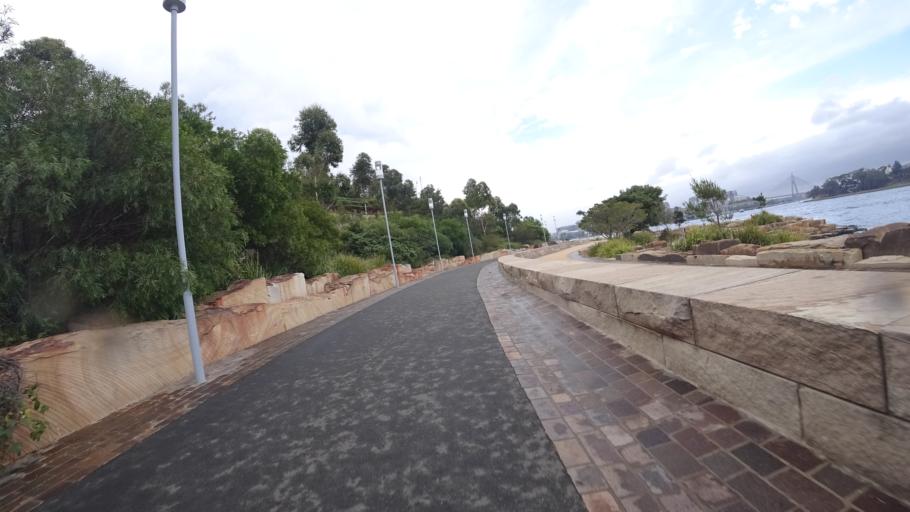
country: AU
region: New South Wales
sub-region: Leichhardt
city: Balmain East
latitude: -33.8570
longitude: 151.2006
